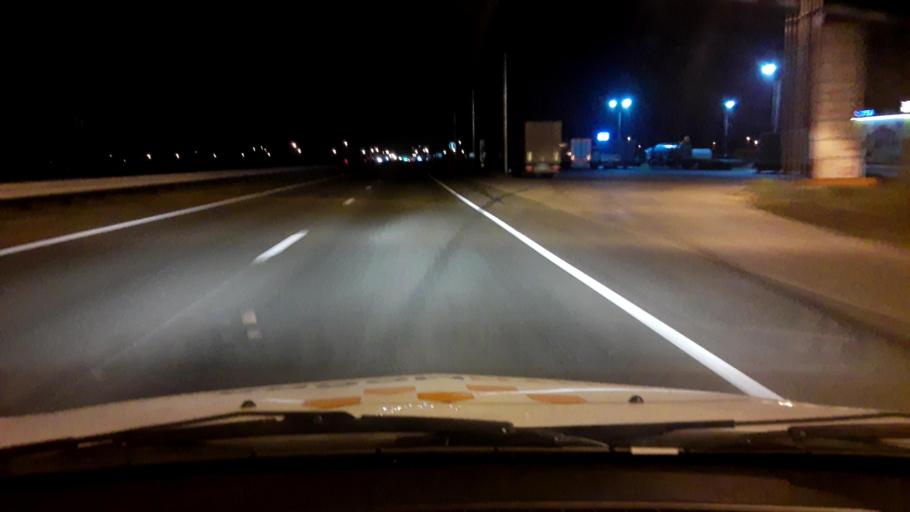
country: RU
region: Bashkortostan
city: Kabakovo
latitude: 54.4870
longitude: 55.9078
